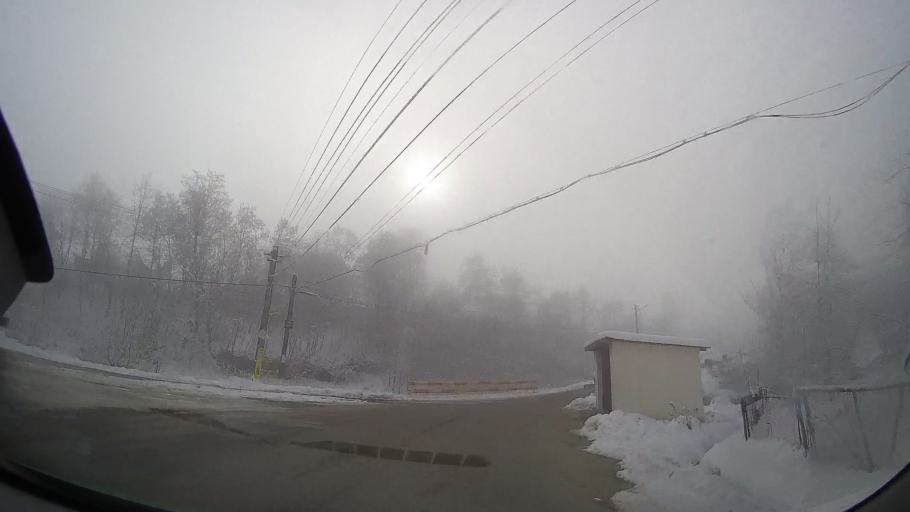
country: RO
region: Iasi
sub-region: Comuna Valea Seaca
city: Topile
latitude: 47.2610
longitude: 26.6678
